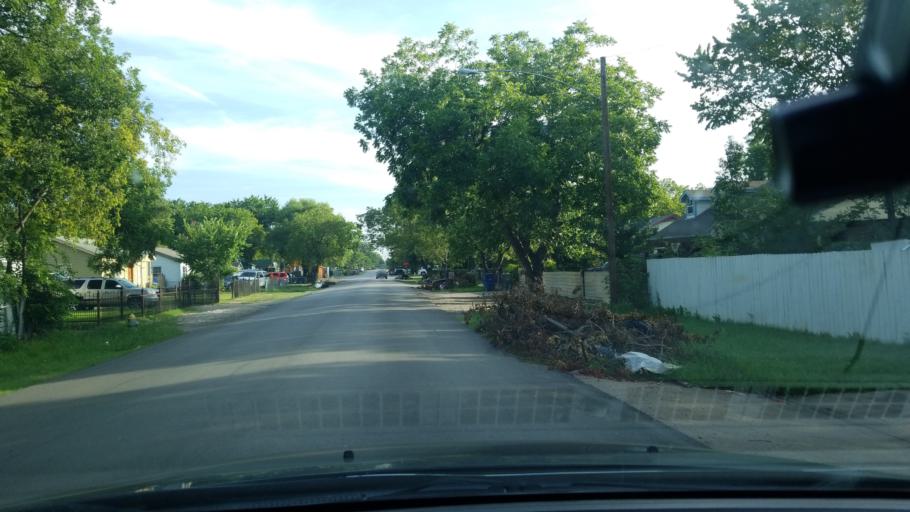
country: US
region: Texas
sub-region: Dallas County
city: Balch Springs
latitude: 32.7240
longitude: -96.6884
